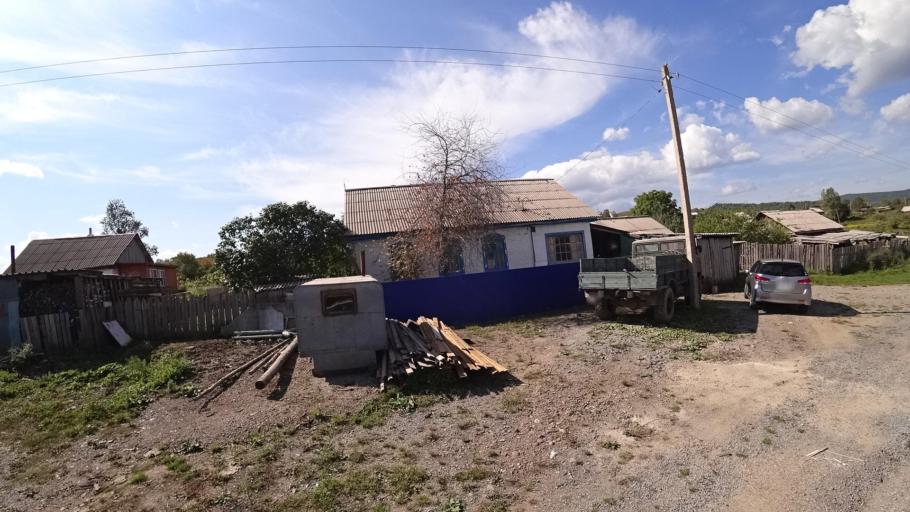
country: RU
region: Jewish Autonomous Oblast
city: Londoko
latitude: 49.0093
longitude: 131.8718
